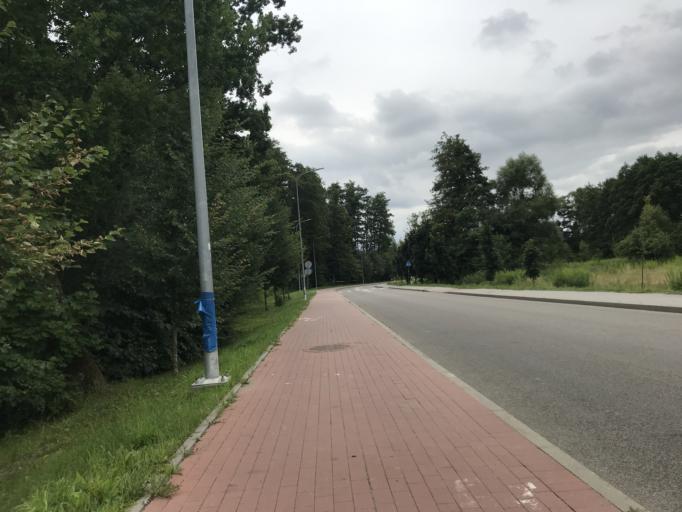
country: PL
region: Warmian-Masurian Voivodeship
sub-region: Powiat elblaski
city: Gronowo Gorne
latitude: 54.1710
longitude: 19.4415
